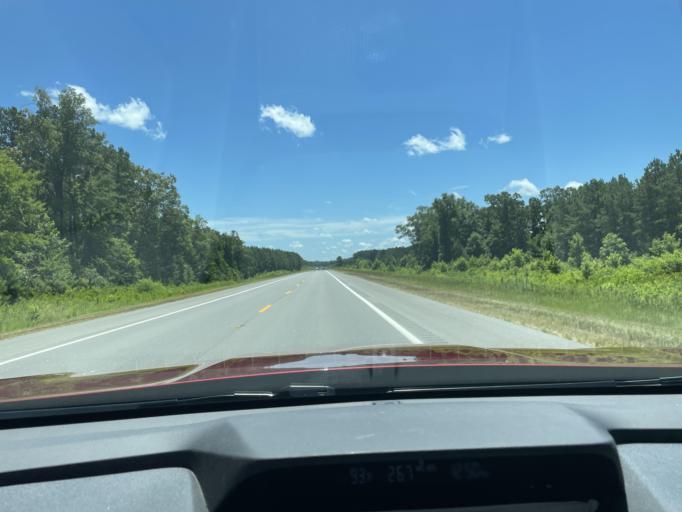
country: US
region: Arkansas
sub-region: Lincoln County
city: Star City
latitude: 33.9544
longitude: -91.9046
